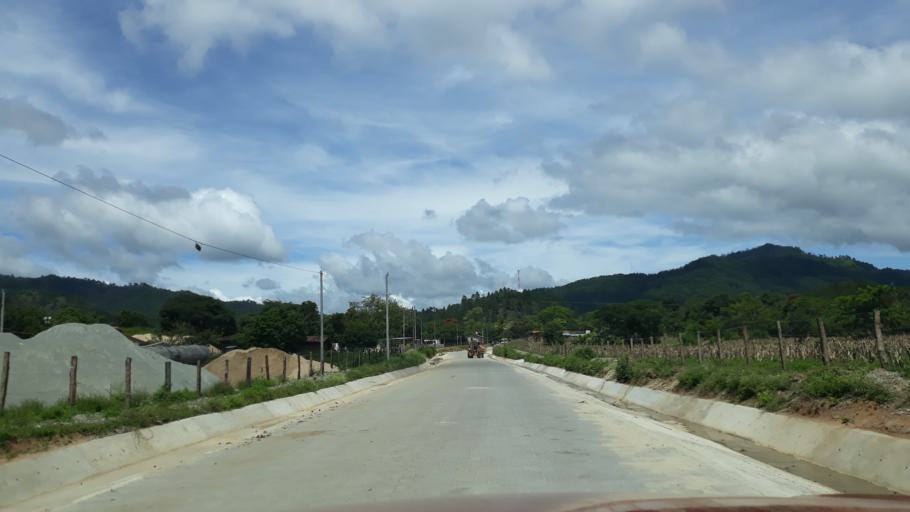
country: HN
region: El Paraiso
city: Santa Cruz
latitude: 13.7278
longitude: -86.6225
